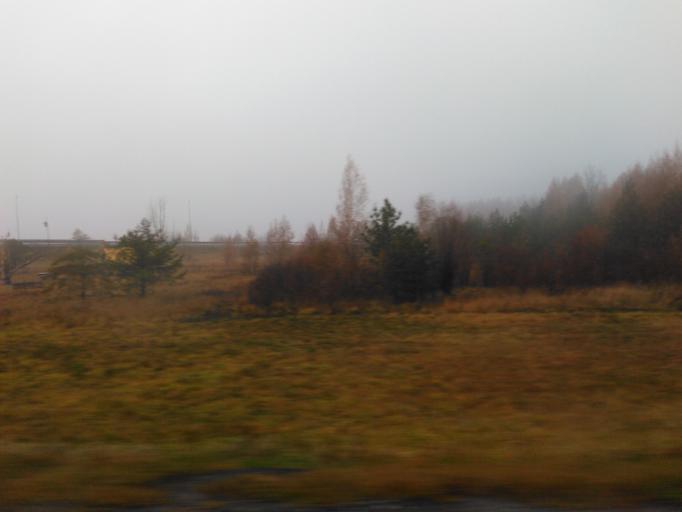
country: RU
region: Tatarstan
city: Sviyazhsk
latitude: 55.7404
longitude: 48.7872
